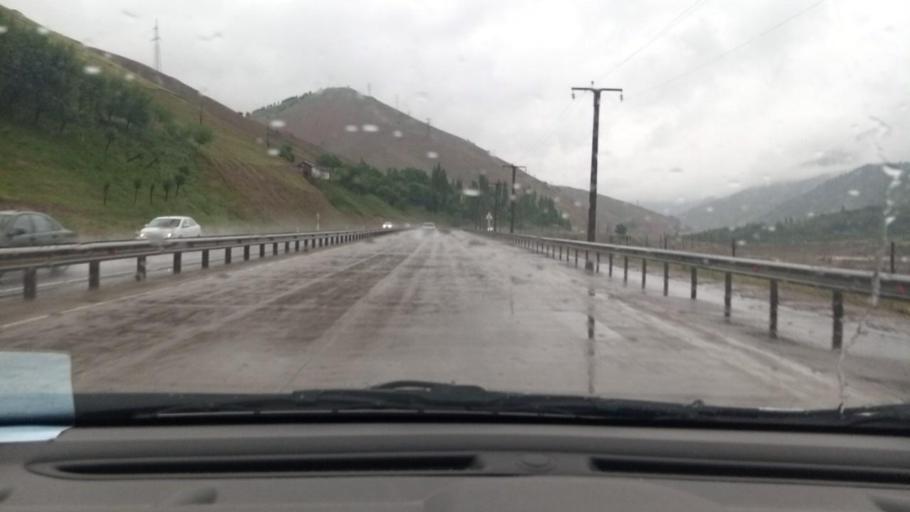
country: UZ
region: Toshkent
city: Angren
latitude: 41.1440
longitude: 70.4053
